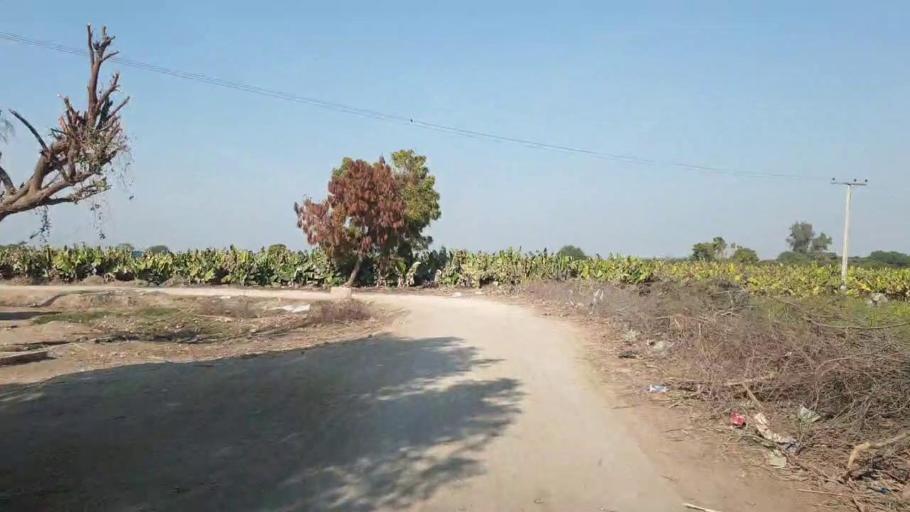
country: PK
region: Sindh
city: Chambar
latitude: 25.3284
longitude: 68.7597
